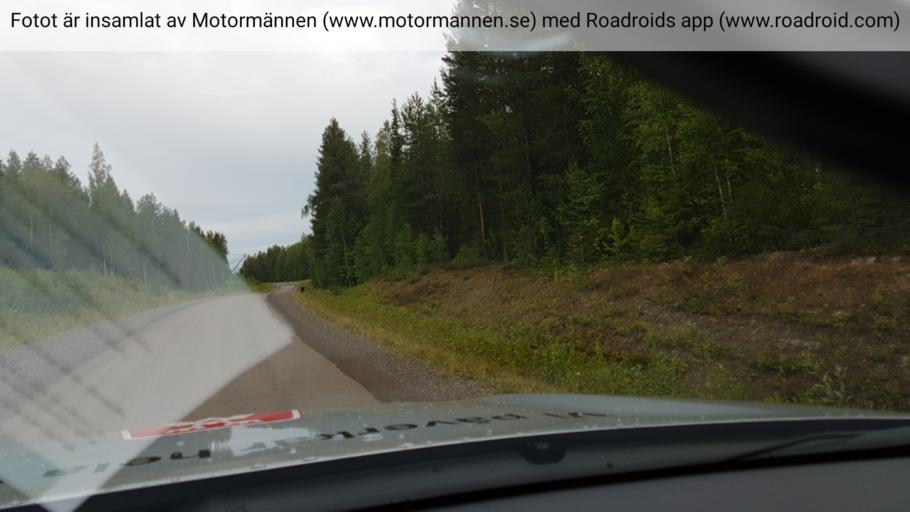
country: SE
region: Norrbotten
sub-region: Alvsbyns Kommun
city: AElvsbyn
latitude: 65.9984
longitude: 21.1626
